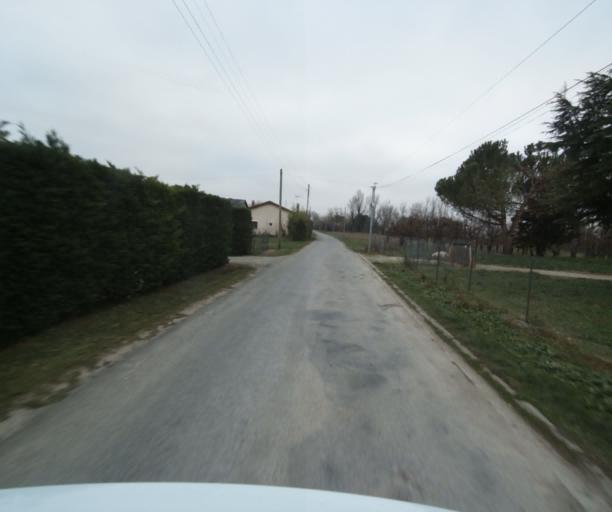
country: FR
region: Midi-Pyrenees
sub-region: Departement du Tarn-et-Garonne
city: Moissac
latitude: 44.1066
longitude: 1.1182
